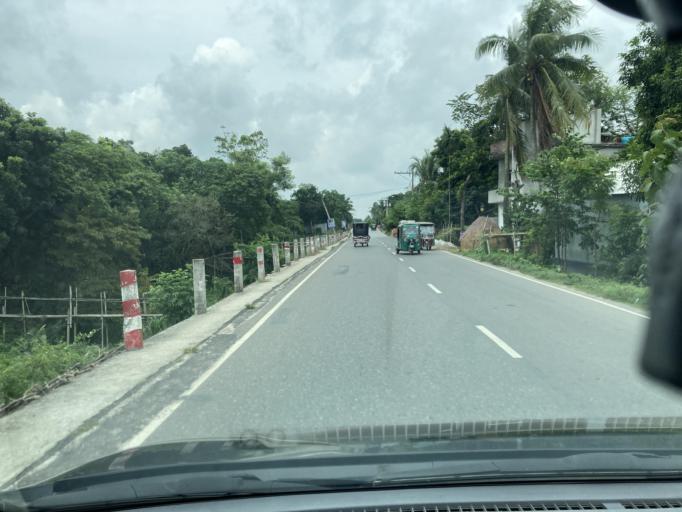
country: BD
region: Dhaka
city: Azimpur
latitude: 23.8058
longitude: 90.2127
